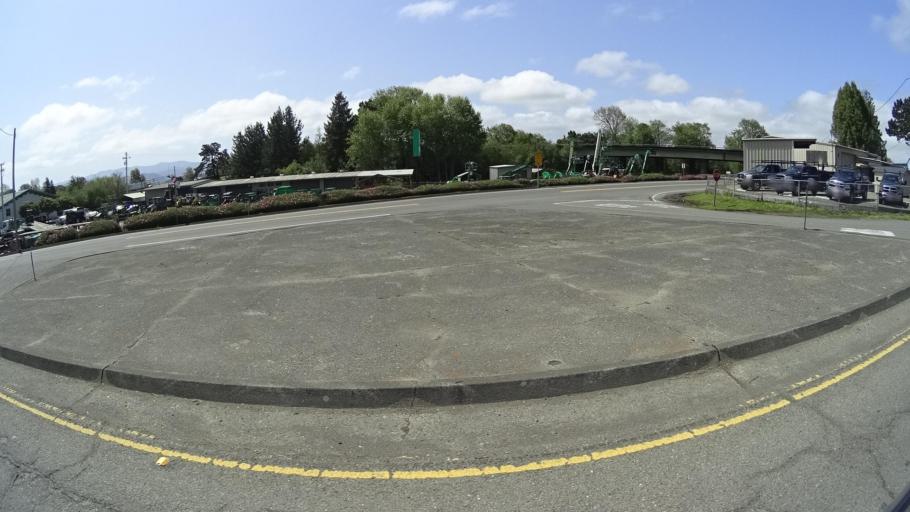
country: US
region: California
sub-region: Humboldt County
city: Fortuna
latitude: 40.6001
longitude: -124.1665
